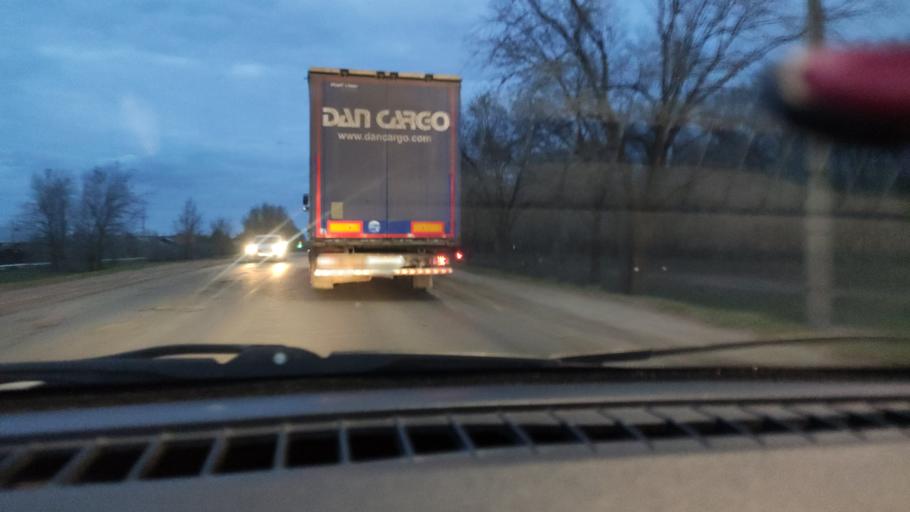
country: RU
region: Orenburg
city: Tatarskaya Kargala
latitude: 51.8746
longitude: 55.1464
